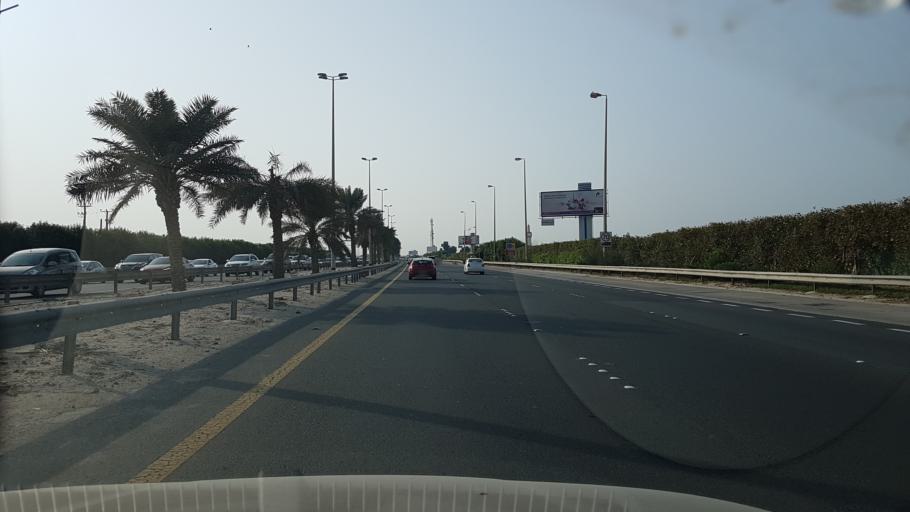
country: BH
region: Northern
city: Madinat `Isa
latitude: 26.1734
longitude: 50.5023
